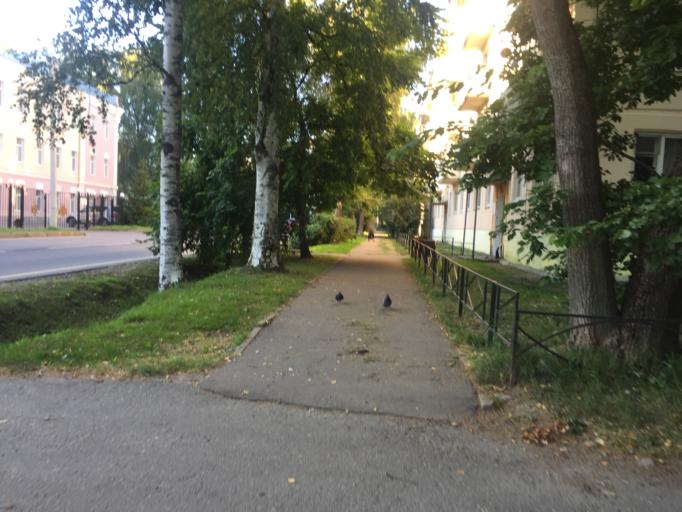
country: RU
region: Leningrad
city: Murino
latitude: 60.0381
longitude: 30.4652
